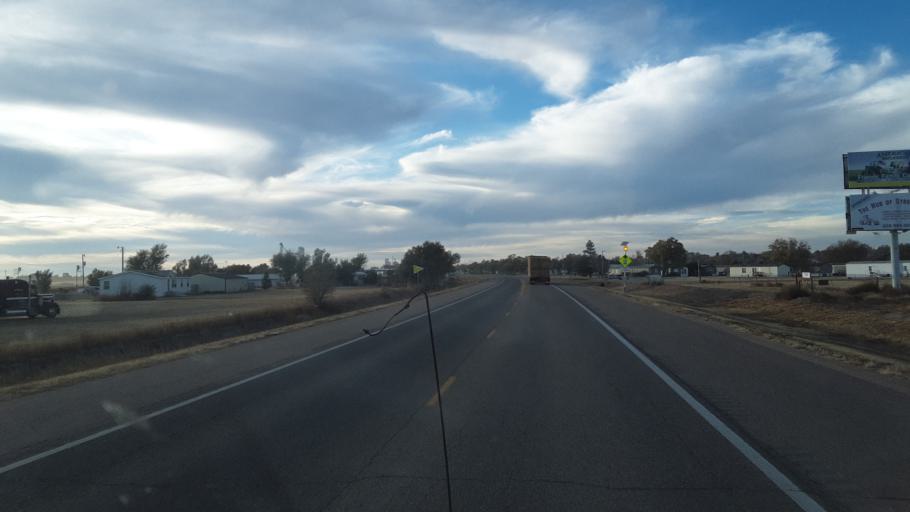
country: US
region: Kansas
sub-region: Hamilton County
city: Syracuse
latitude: 37.9766
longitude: -101.7372
